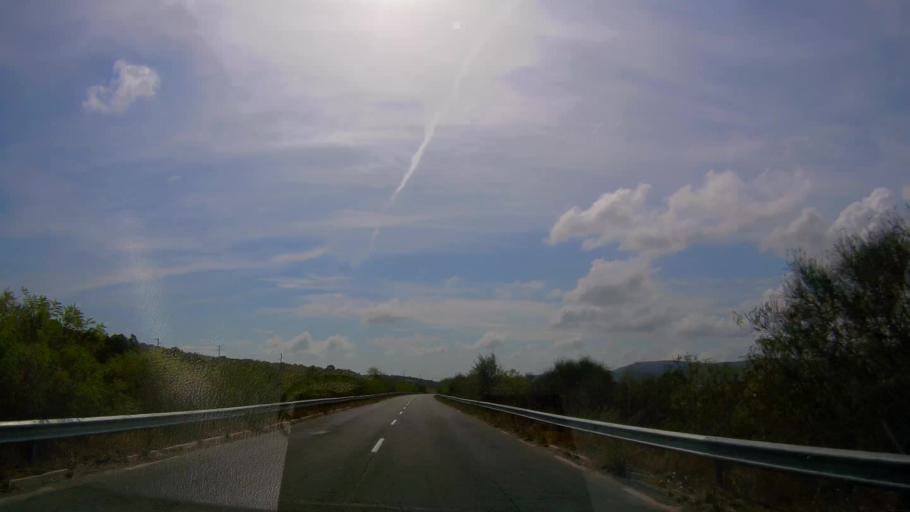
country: BG
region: Burgas
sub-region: Obshtina Sozopol
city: Sozopol
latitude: 42.3844
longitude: 27.6801
